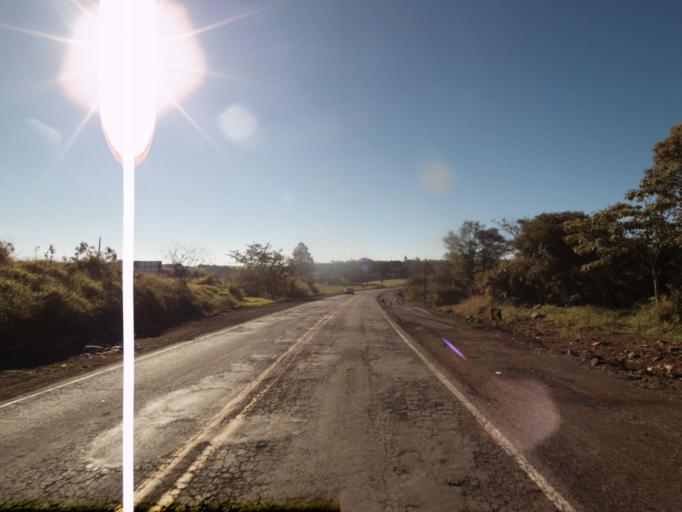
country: AR
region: Misiones
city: Bernardo de Irigoyen
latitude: -26.6490
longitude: -53.5189
